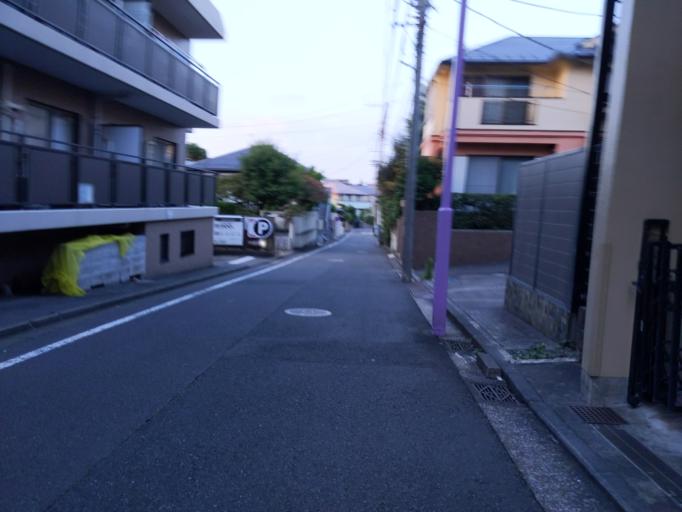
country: JP
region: Kanagawa
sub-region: Kawasaki-shi
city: Kawasaki
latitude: 35.5542
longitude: 139.6436
